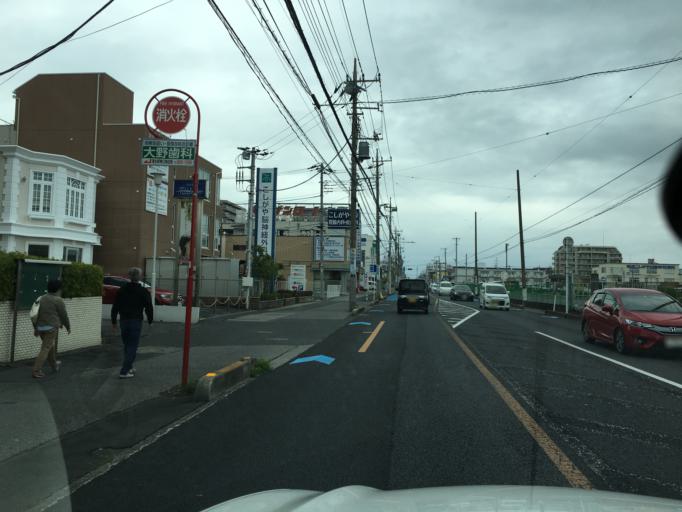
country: JP
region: Saitama
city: Koshigaya
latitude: 35.8673
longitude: 139.7947
